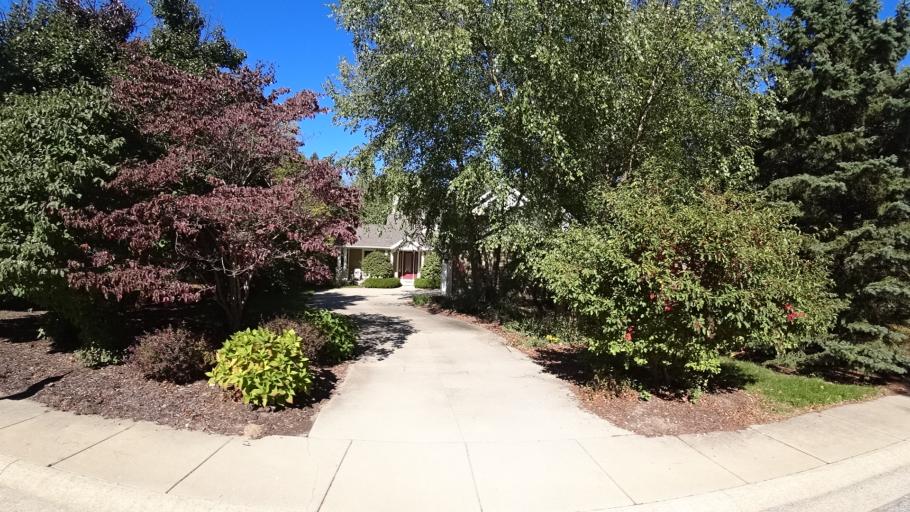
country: US
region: Indiana
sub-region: LaPorte County
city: Long Beach
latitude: 41.7471
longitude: -86.8279
